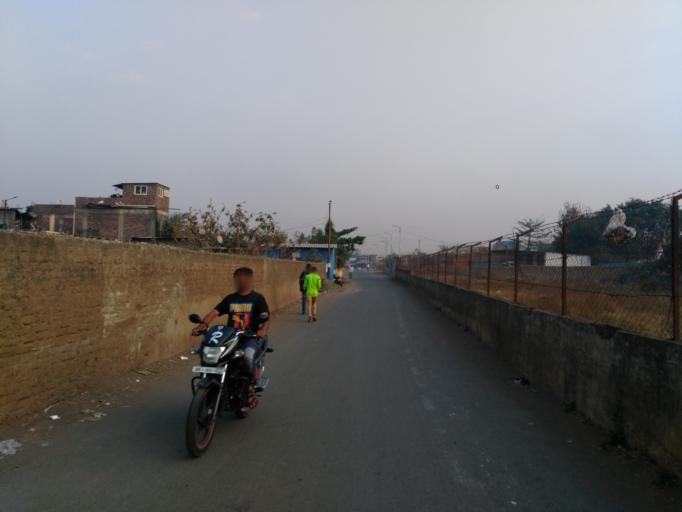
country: IN
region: Maharashtra
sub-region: Pune Division
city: Pune
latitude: 18.4592
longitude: 73.8729
